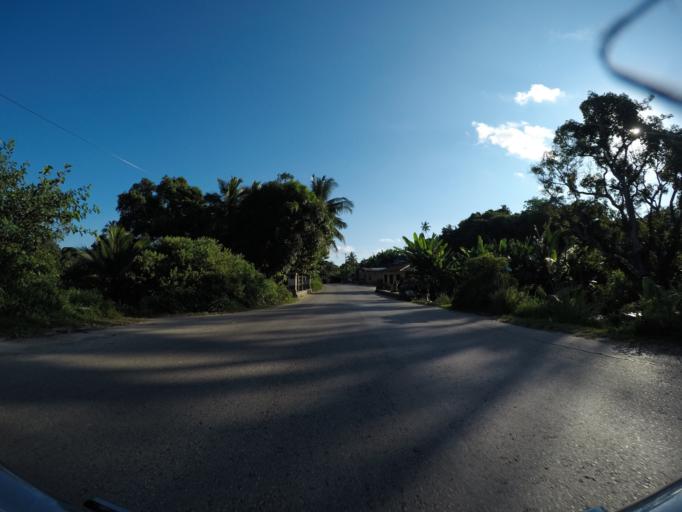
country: TZ
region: Pemba South
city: Chake Chake
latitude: -5.3084
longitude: 39.7451
